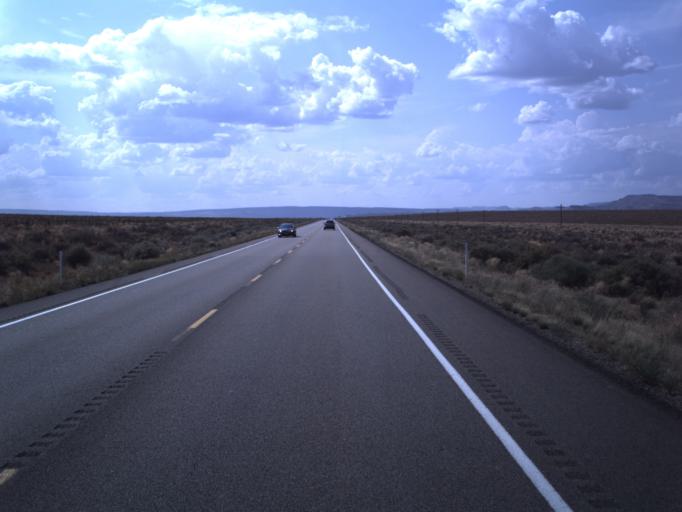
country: US
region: Arizona
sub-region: Coconino County
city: Page
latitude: 37.0926
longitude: -111.7393
